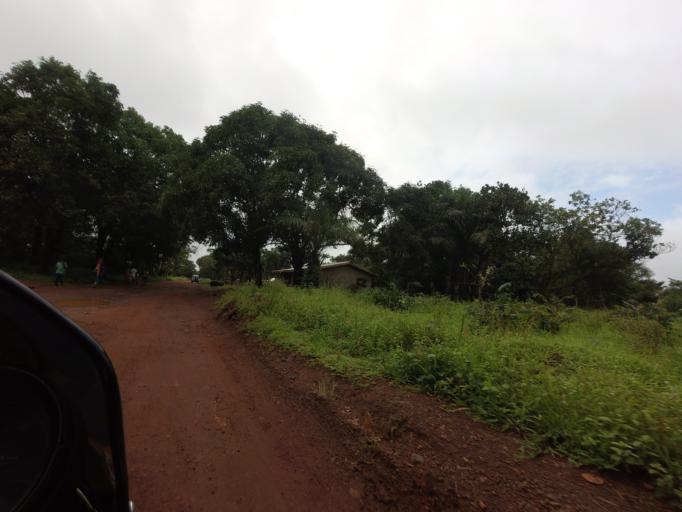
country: SL
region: Northern Province
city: Kambia
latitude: 9.1292
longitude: -12.8987
